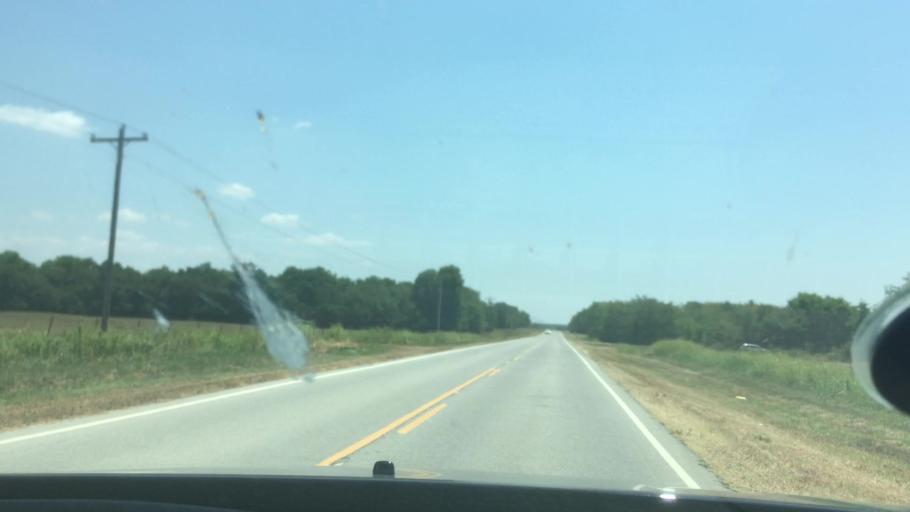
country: US
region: Oklahoma
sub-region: Coal County
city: Coalgate
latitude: 34.5862
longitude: -96.4164
